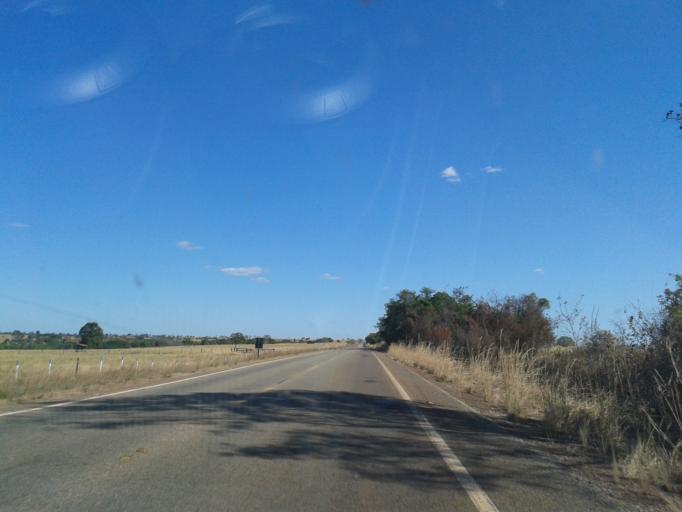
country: BR
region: Goias
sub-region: Mozarlandia
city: Mozarlandia
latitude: -14.3667
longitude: -50.4289
